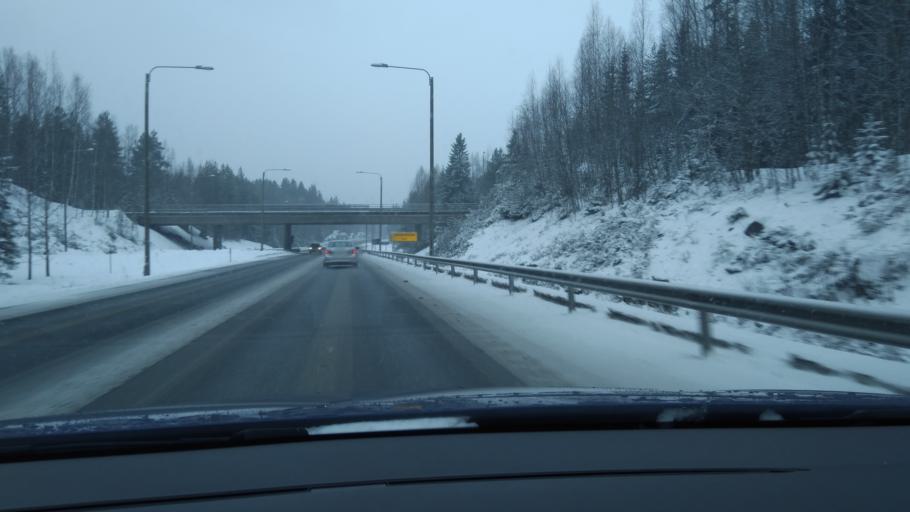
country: FI
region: Pirkanmaa
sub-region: Tampere
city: Kangasala
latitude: 61.5332
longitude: 23.9530
